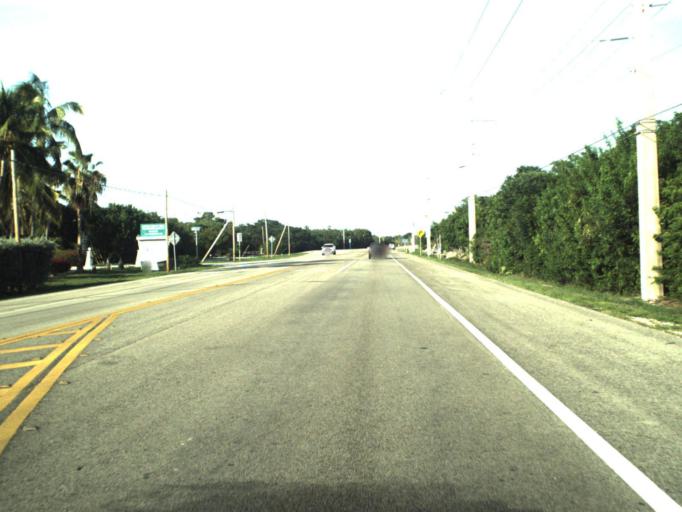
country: US
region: Florida
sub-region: Monroe County
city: Marathon
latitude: 24.7693
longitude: -80.9416
